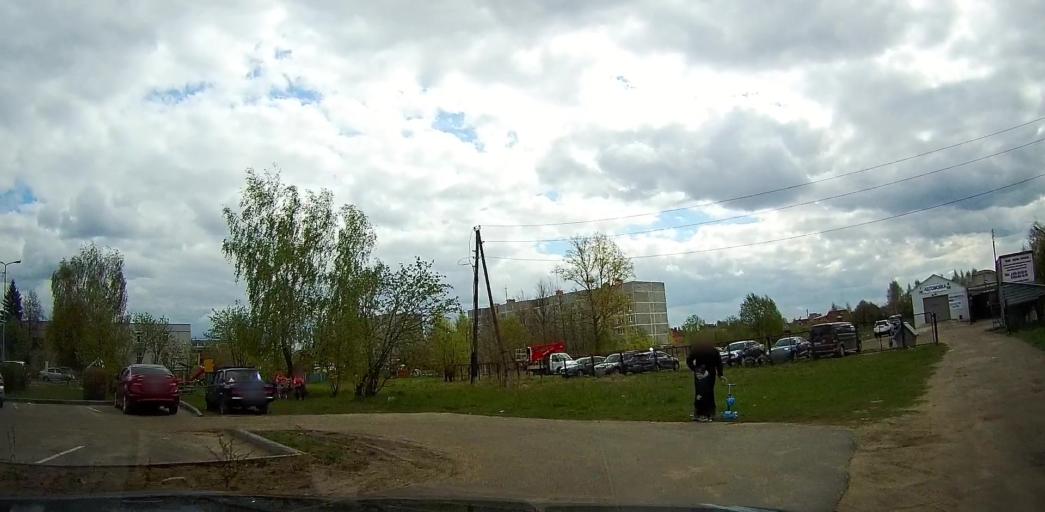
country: RU
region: Moskovskaya
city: Ashitkovo
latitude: 55.4356
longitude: 38.5800
